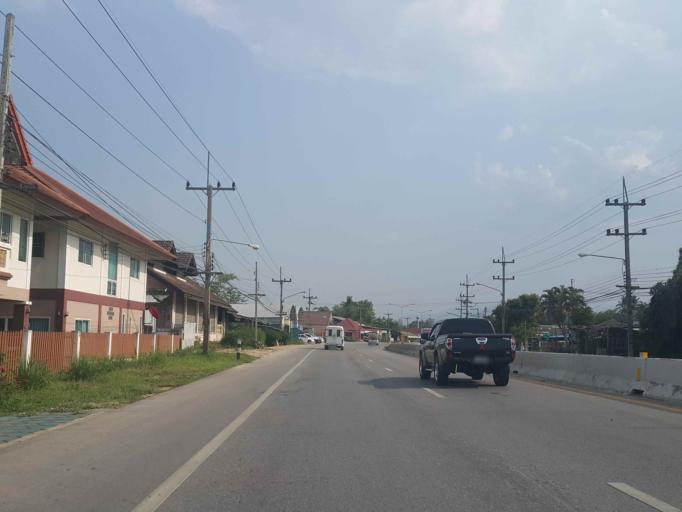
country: TH
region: Chiang Mai
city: Mae Taeng
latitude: 19.0371
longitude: 98.9466
